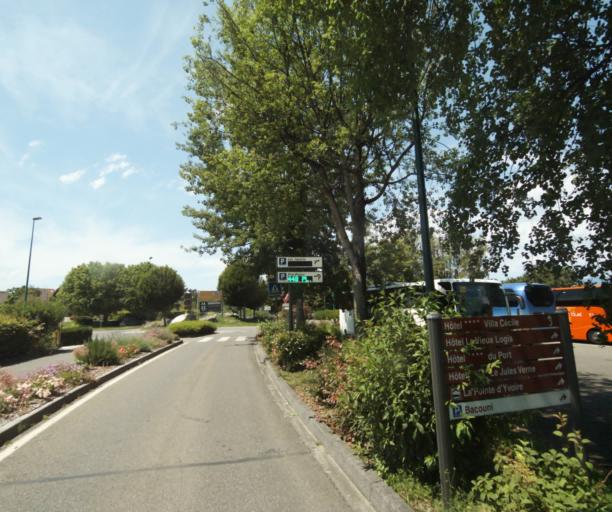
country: FR
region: Rhone-Alpes
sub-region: Departement de la Haute-Savoie
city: Messery
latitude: 46.3682
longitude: 6.3260
